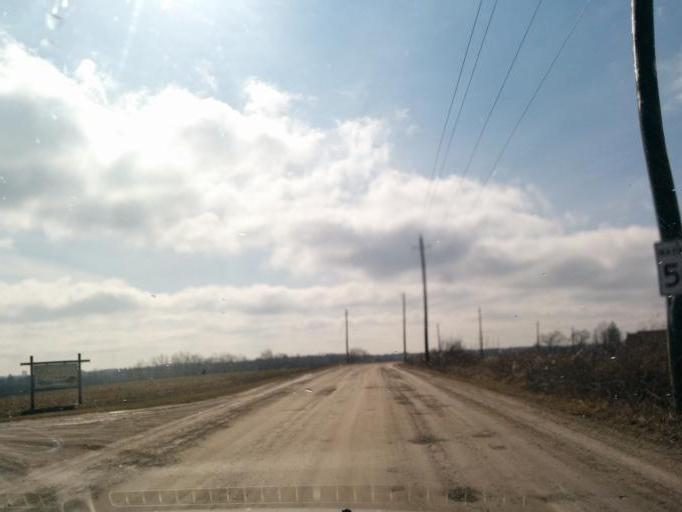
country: CA
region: Ontario
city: Waterloo
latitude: 43.5096
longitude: -80.4683
